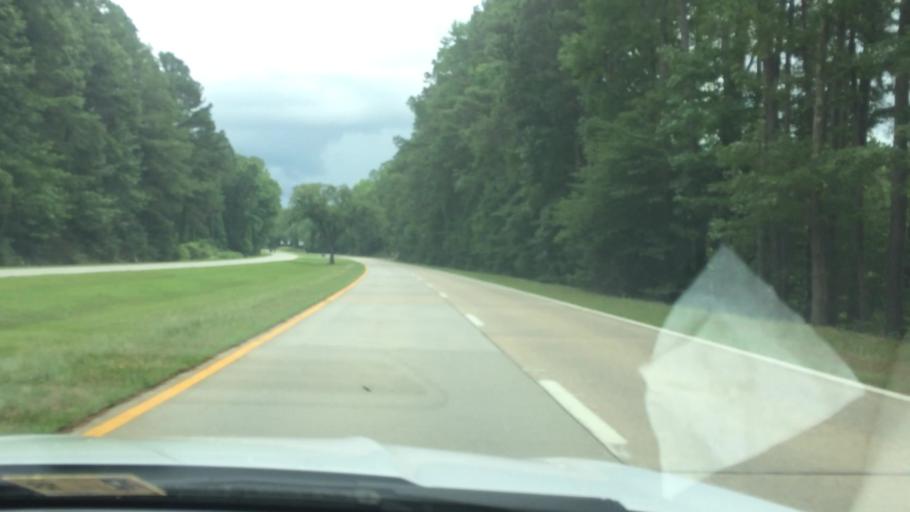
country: US
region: Virginia
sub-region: King William County
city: West Point
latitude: 37.4065
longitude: -76.8522
